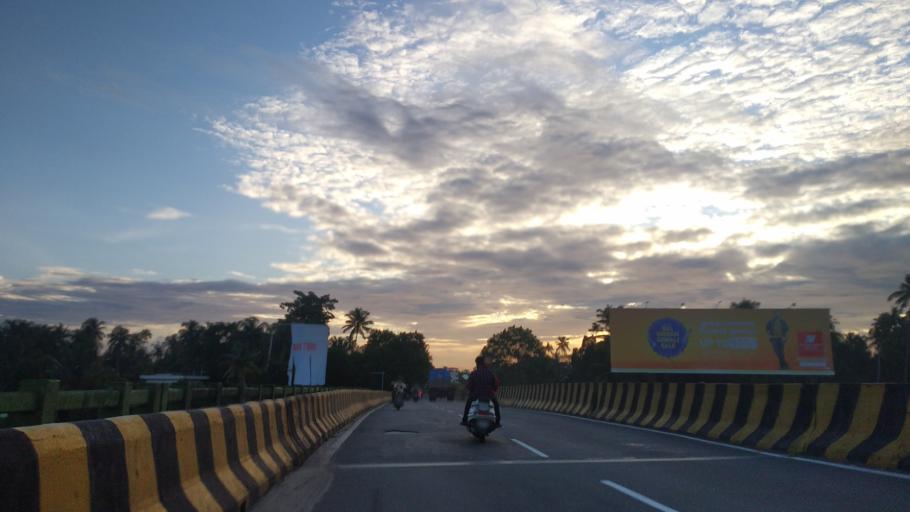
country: IN
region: Kerala
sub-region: Ernakulam
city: Elur
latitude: 10.0519
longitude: 76.2795
